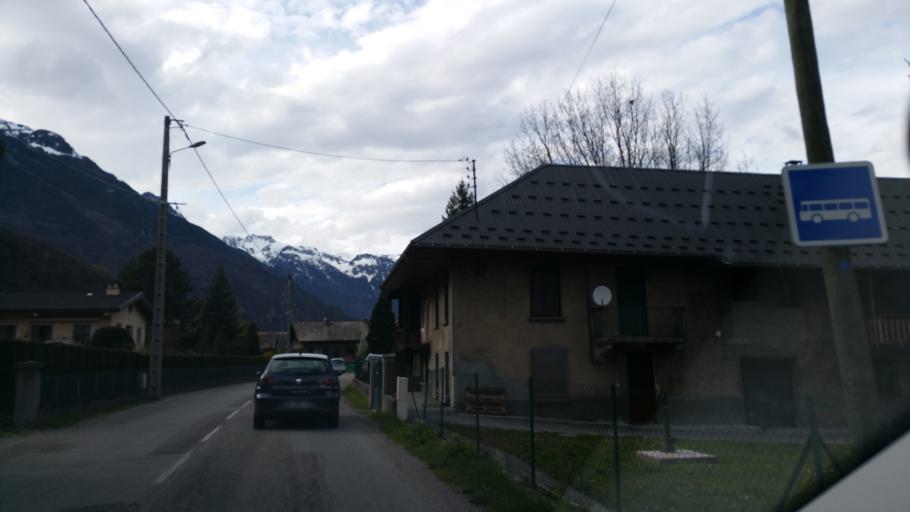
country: FR
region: Rhone-Alpes
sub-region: Departement de la Savoie
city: La Chambre
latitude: 45.3331
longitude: 6.3087
